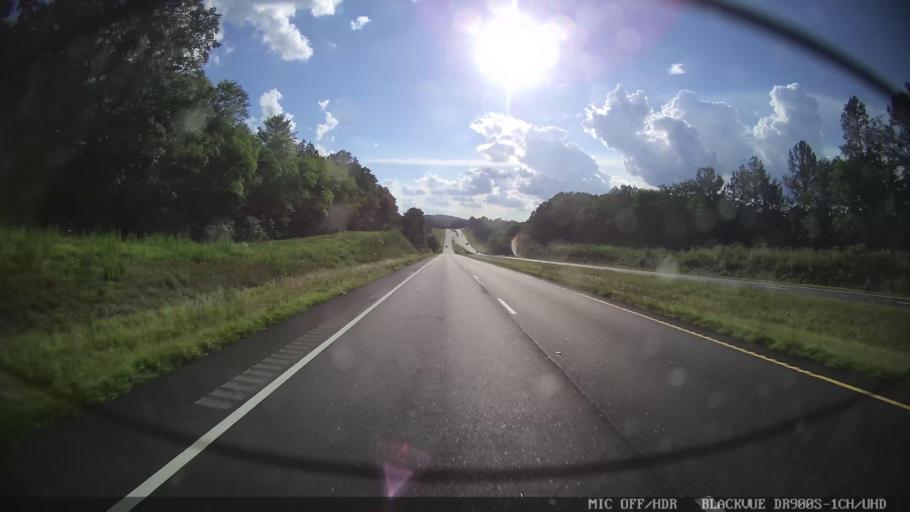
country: US
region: Georgia
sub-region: Floyd County
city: Lindale
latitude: 34.2060
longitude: -85.0724
